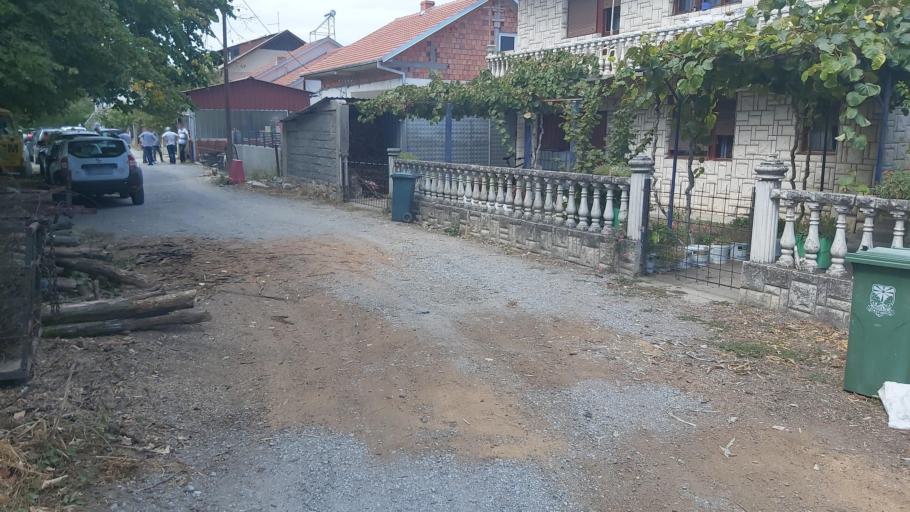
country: MK
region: Demir Kapija
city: Demir Kapija
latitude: 41.4087
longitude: 22.2409
